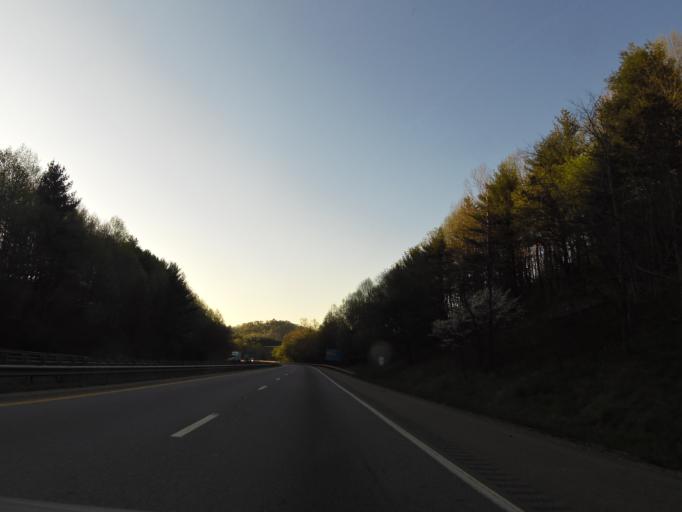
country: US
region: North Carolina
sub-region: Haywood County
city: Lake Junaluska
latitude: 35.5636
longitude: -82.9514
